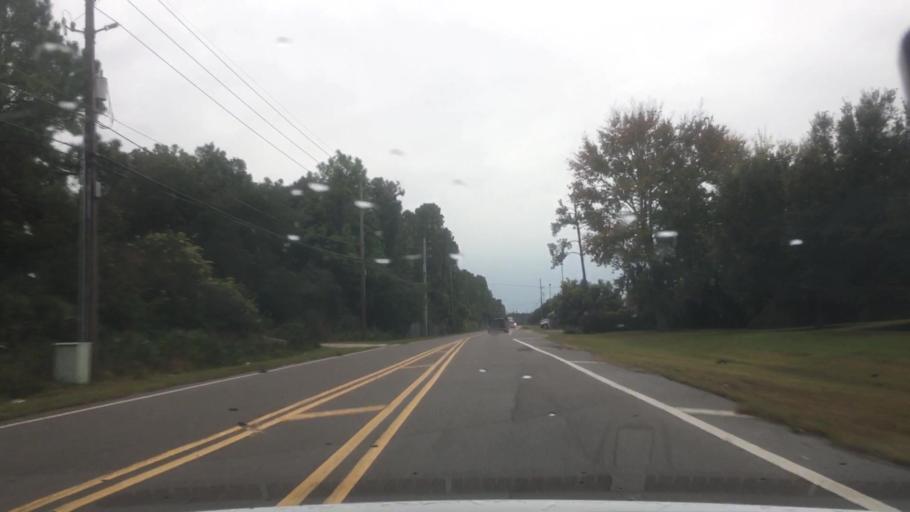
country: US
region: Florida
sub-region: Duval County
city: Jacksonville
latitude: 30.4492
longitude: -81.5582
